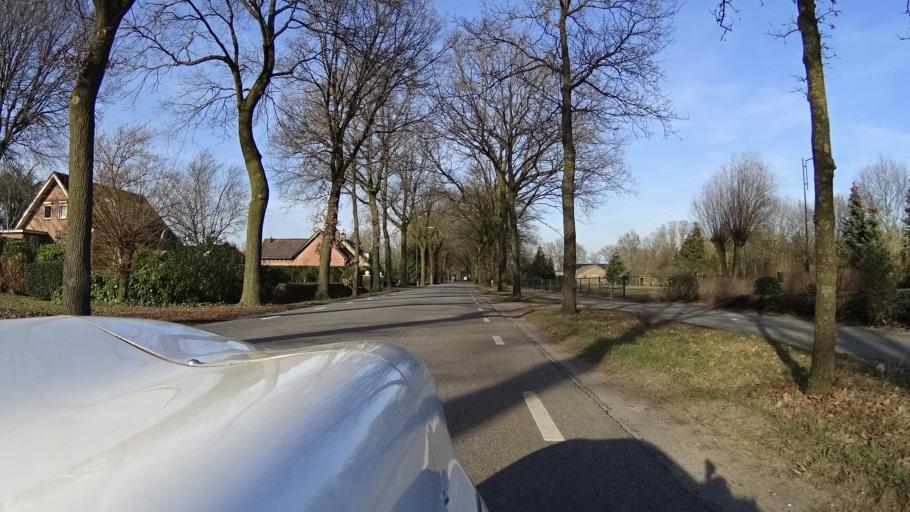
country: NL
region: North Brabant
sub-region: Gemeente Veghel
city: Erp
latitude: 51.5872
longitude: 5.6158
